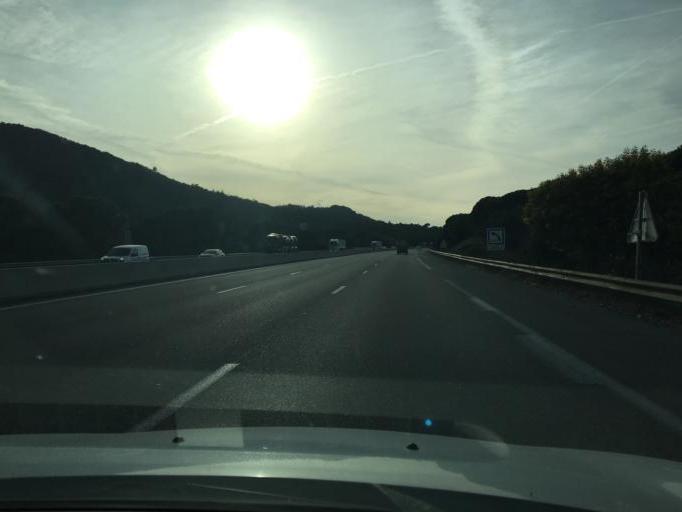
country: FR
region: Provence-Alpes-Cote d'Azur
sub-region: Departement du Var
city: Le Muy
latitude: 43.4566
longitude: 6.5450
